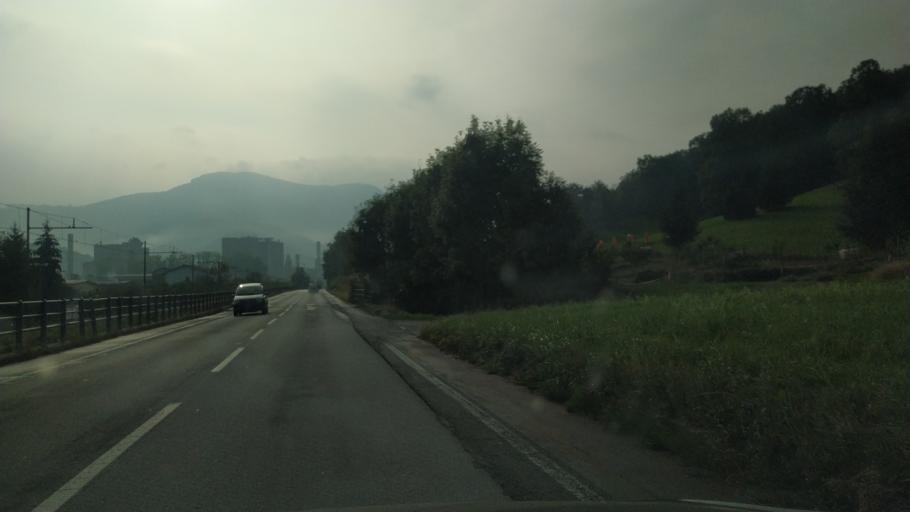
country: IT
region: Piedmont
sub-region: Provincia di Cuneo
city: Roccavione
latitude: 44.3062
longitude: 7.4974
